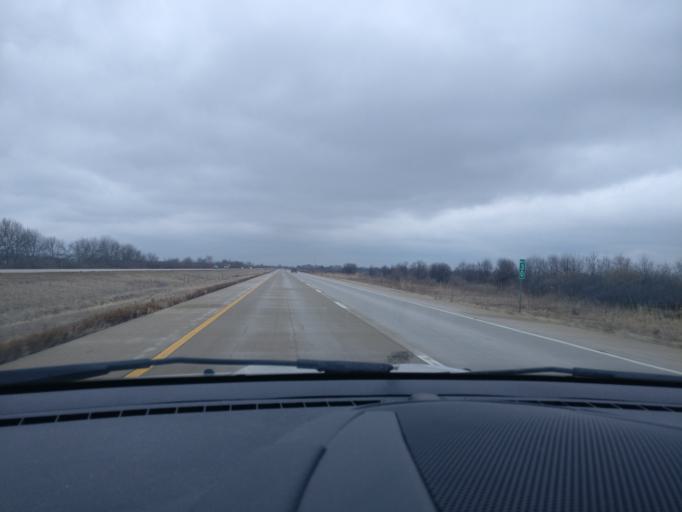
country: US
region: Illinois
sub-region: Whiteside County
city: Prophetstown
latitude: 41.7381
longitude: -89.8895
